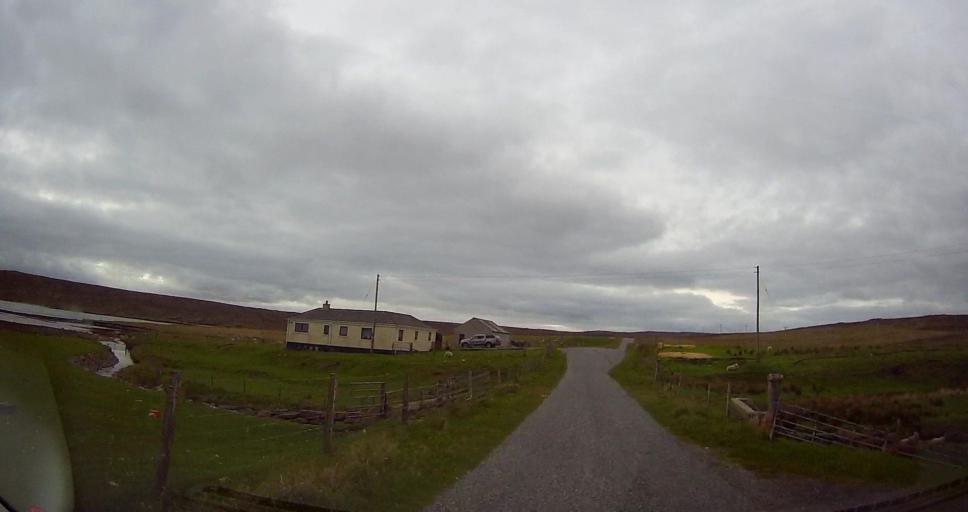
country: GB
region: Scotland
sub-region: Shetland Islands
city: Shetland
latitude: 60.5044
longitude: -1.1029
